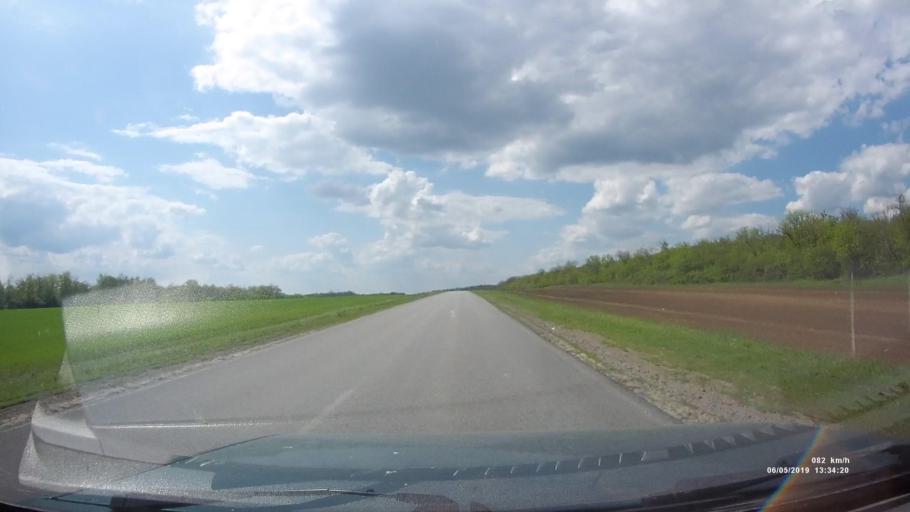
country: RU
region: Rostov
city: Ust'-Donetskiy
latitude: 47.6926
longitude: 40.7645
